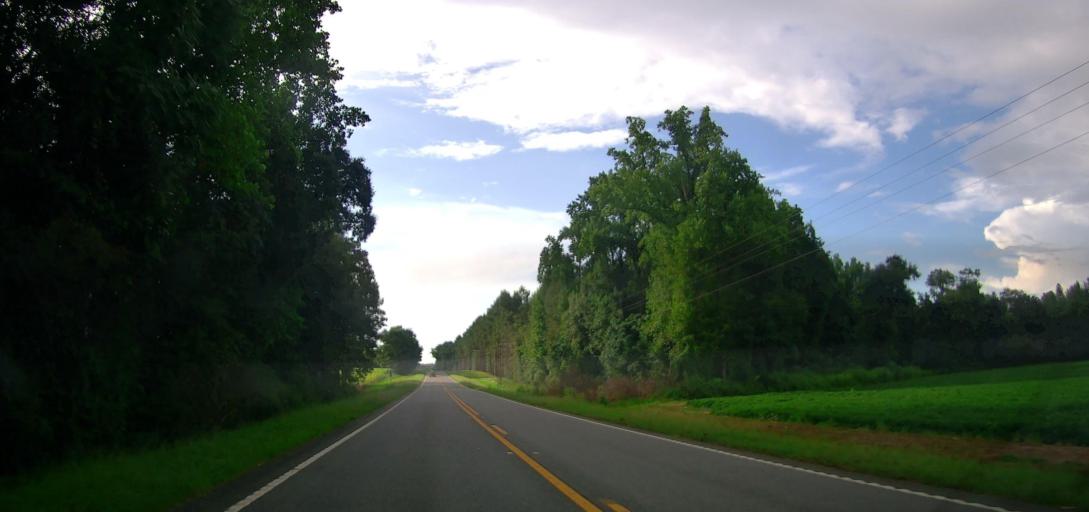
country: US
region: Georgia
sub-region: Coffee County
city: Nicholls
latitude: 31.3207
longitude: -82.5758
